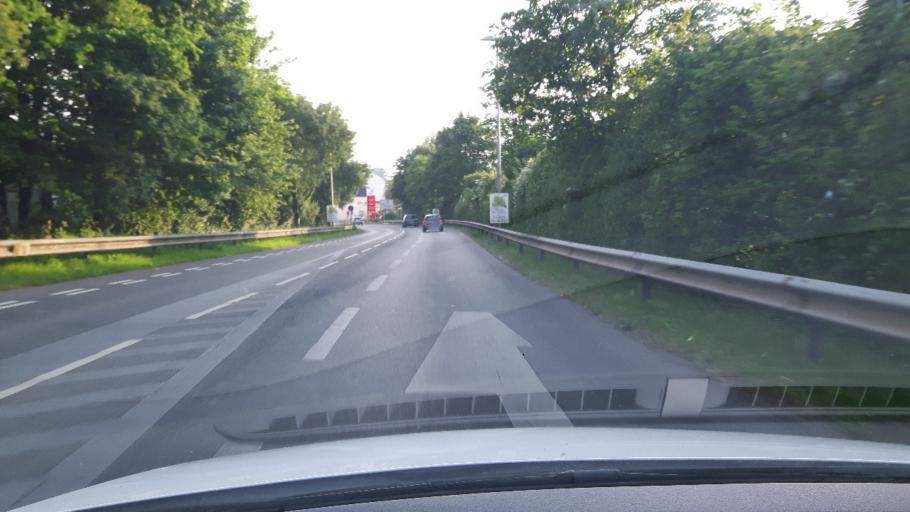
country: DE
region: North Rhine-Westphalia
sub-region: Regierungsbezirk Koln
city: Siegburg
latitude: 50.8087
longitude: 7.2339
